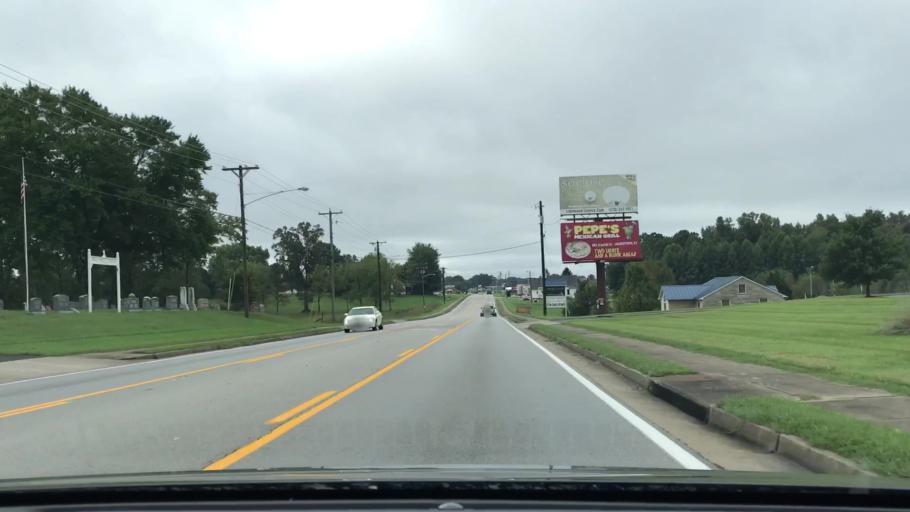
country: US
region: Kentucky
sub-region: Russell County
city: Jamestown
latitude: 37.0177
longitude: -85.0760
